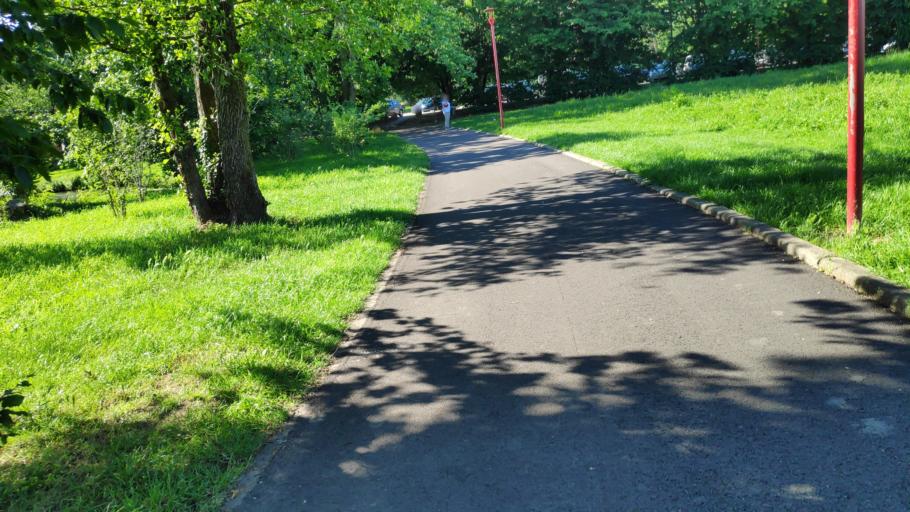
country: IT
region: Lombardy
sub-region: Citta metropolitana di Milano
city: Basiglio
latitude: 45.3571
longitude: 9.1550
